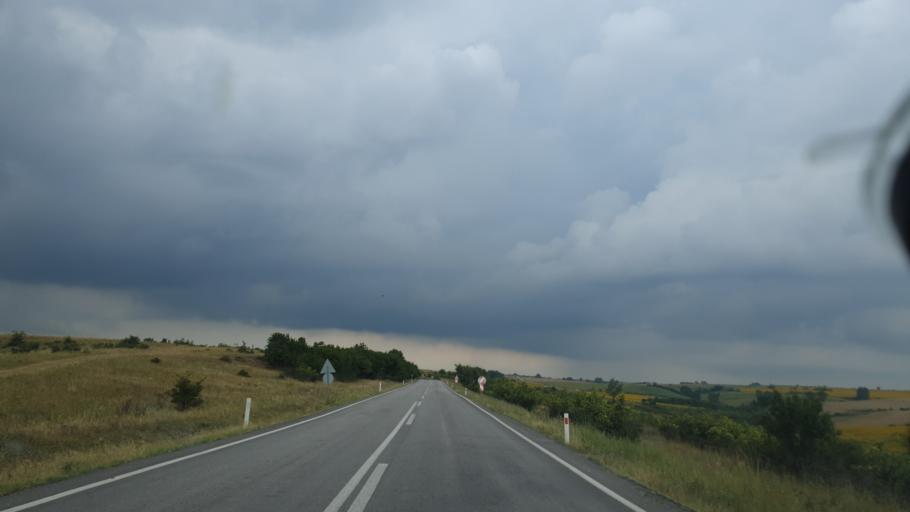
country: TR
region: Tekirdag
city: Hayrabolu
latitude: 41.2217
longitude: 27.0119
